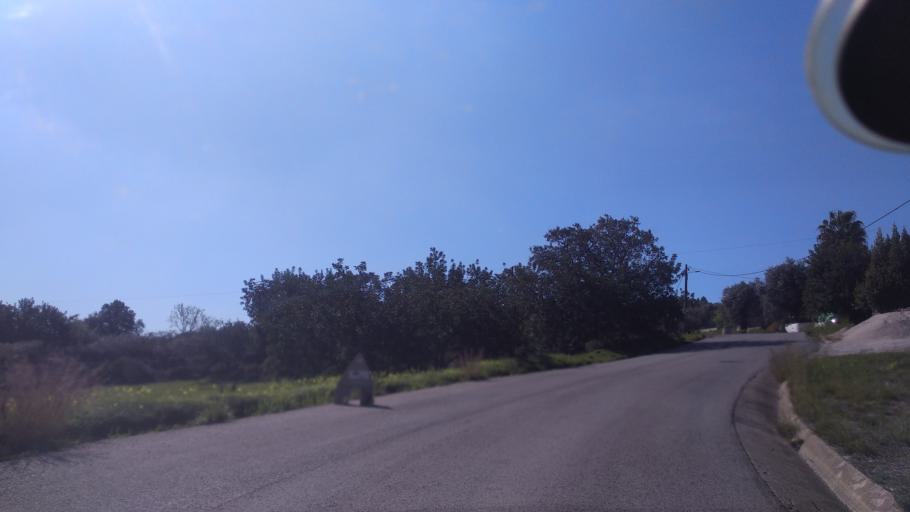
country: PT
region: Faro
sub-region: Faro
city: Santa Barbara de Nexe
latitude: 37.1191
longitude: -7.9250
